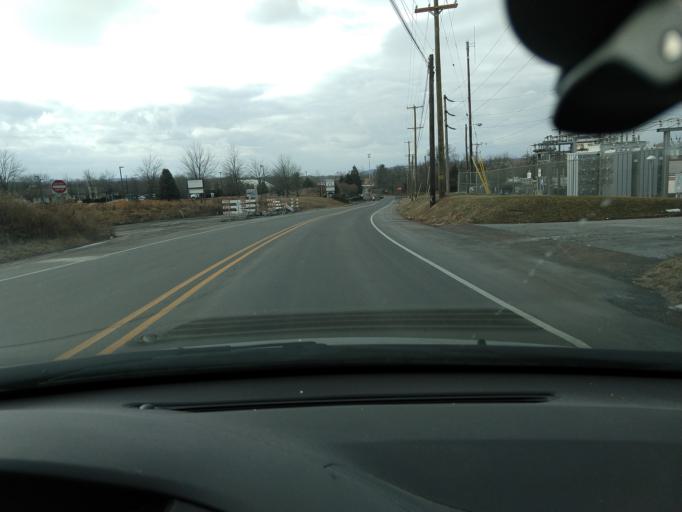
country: US
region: Pennsylvania
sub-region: Chester County
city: Kenilworth
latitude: 40.2345
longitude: -75.6185
